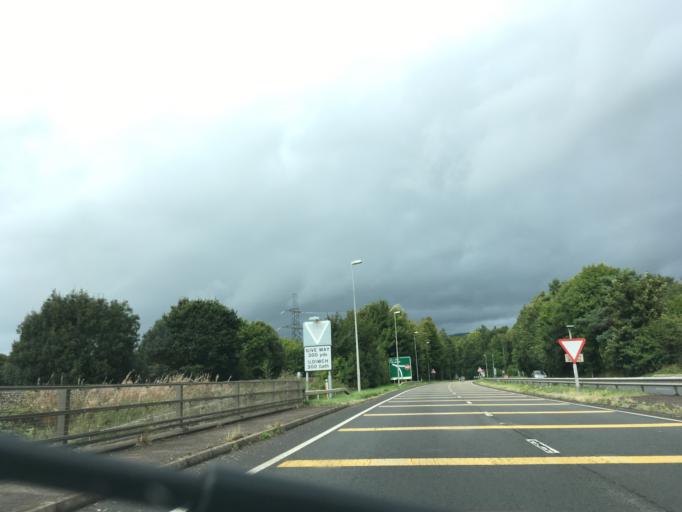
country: GB
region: Wales
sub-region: Monmouthshire
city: Abergavenny
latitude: 51.8051
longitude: -3.0057
